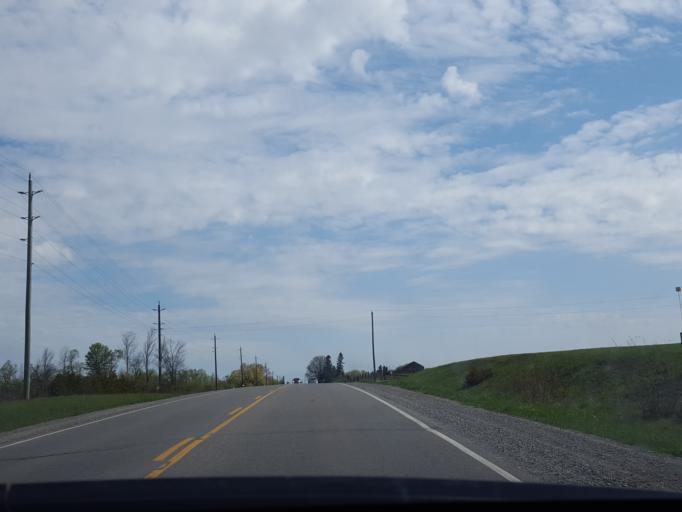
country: CA
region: Ontario
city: Uxbridge
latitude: 44.1493
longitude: -78.9038
